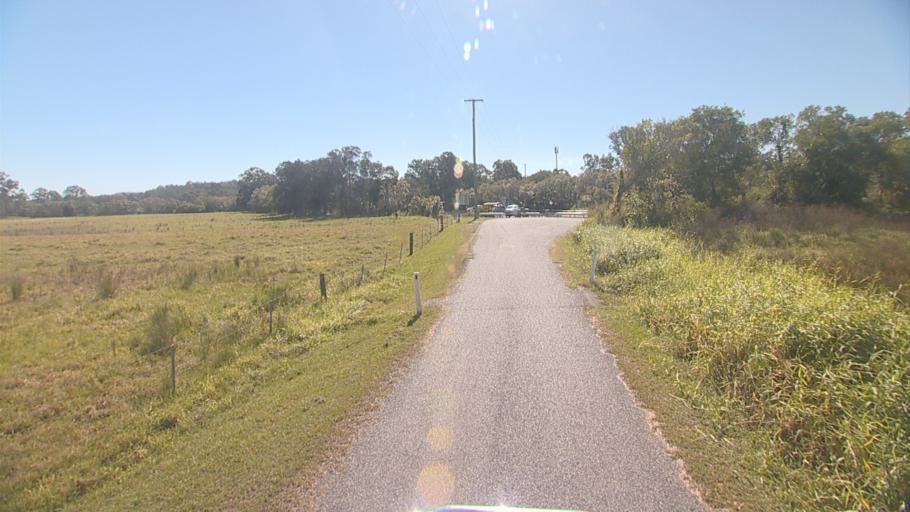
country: AU
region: Queensland
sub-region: Gold Coast
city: Yatala
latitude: -27.6819
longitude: 153.2253
